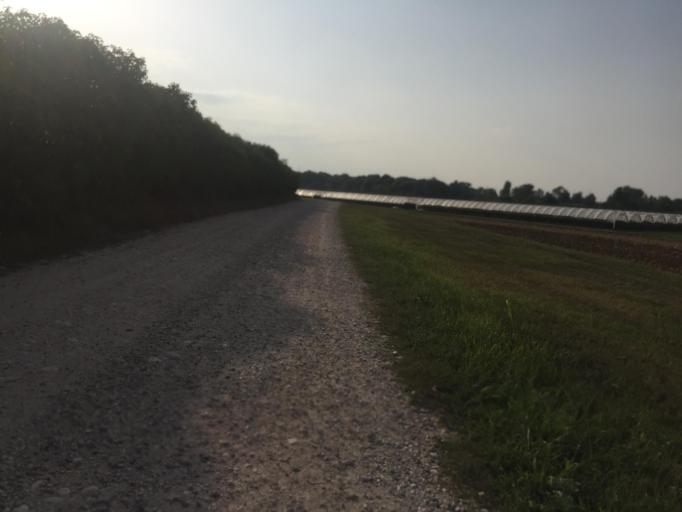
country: IT
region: Veneto
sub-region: Provincia di Verona
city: Campagnola
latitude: 45.3821
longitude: 11.0802
